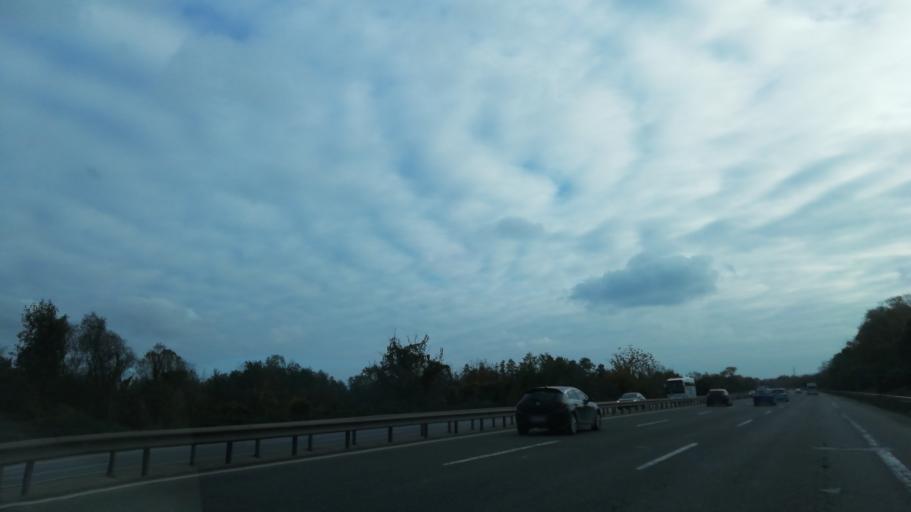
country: TR
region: Kocaeli
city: Derbent
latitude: 40.7051
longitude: 30.1818
